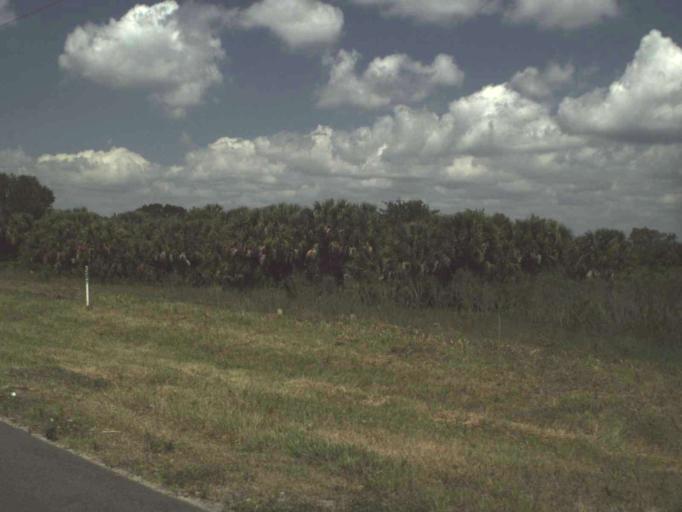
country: US
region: Florida
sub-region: Seminole County
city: Midway
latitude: 28.8149
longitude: -81.1921
